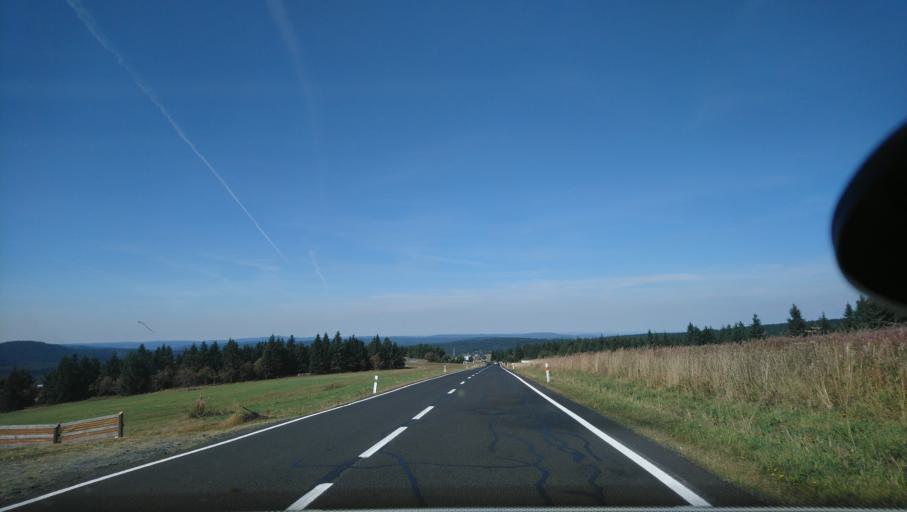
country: DE
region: Saxony
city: Kurort Oberwiesenthal
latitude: 50.4035
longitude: 12.9431
